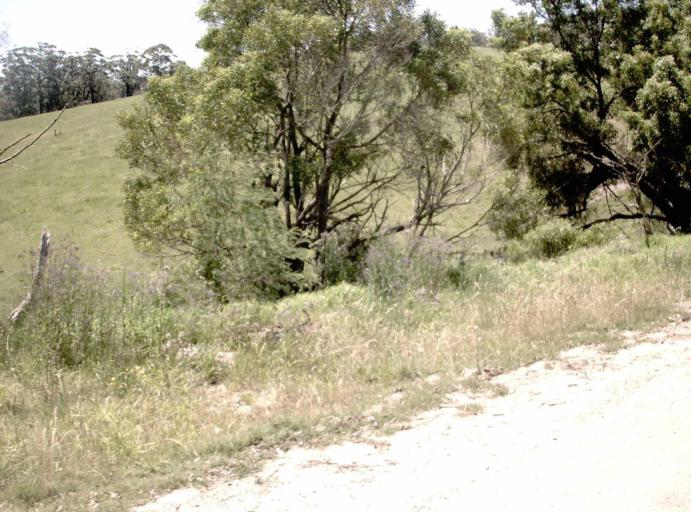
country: AU
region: Victoria
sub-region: East Gippsland
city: Lakes Entrance
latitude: -37.7055
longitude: 148.5527
